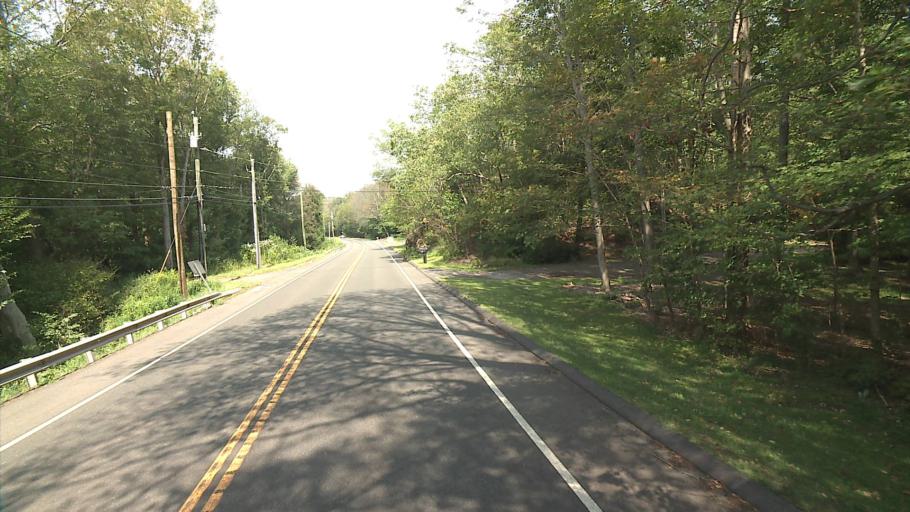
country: US
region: Connecticut
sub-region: Middlesex County
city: Durham
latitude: 41.4473
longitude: -72.6639
